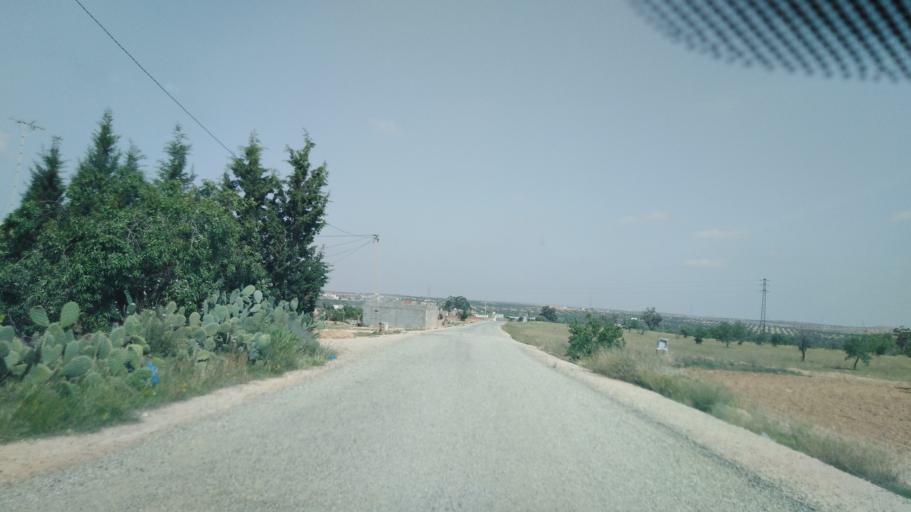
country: TN
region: Safaqis
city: Sfax
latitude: 34.7270
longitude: 10.5727
